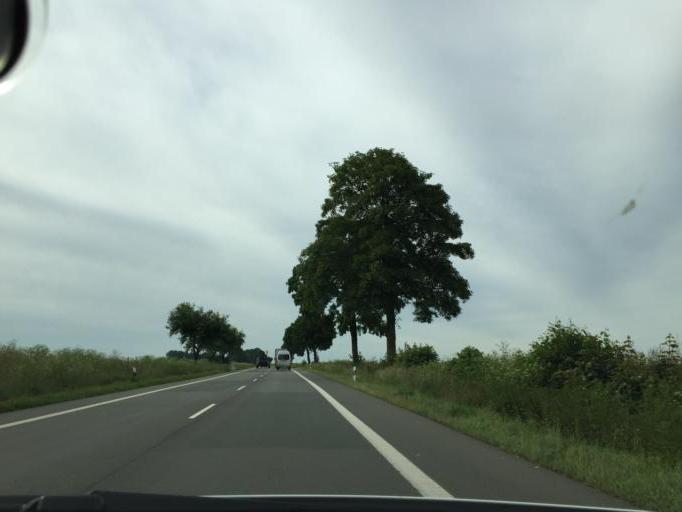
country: DE
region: North Rhine-Westphalia
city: Warburg
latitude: 51.5487
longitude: 9.1322
